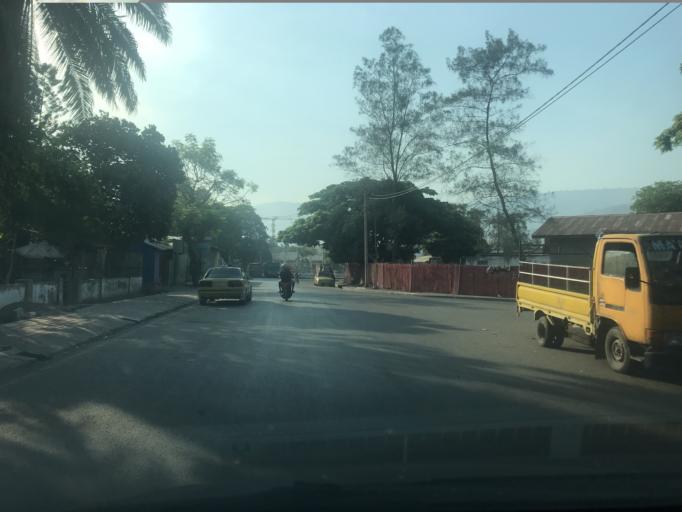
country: TL
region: Dili
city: Dili
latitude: -8.5529
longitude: 125.5714
